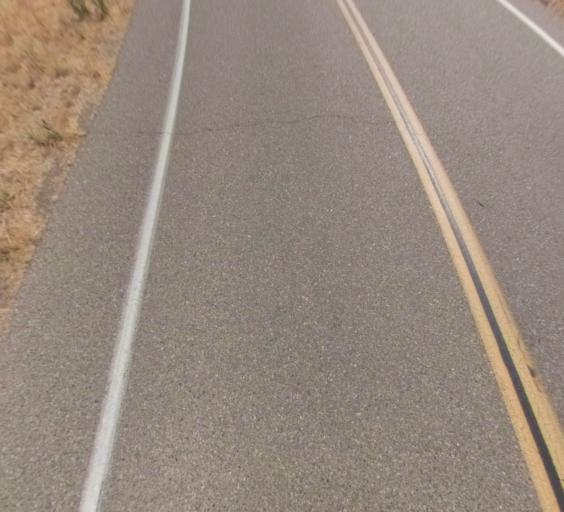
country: US
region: California
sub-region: Madera County
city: Bonadelle Ranchos-Madera Ranchos
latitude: 36.9233
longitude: -119.7752
